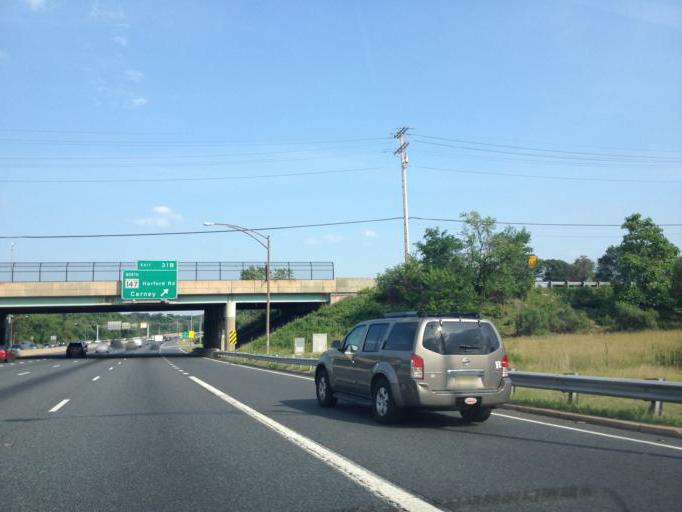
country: US
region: Maryland
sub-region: Baltimore County
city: Carney
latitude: 39.3887
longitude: -76.5314
